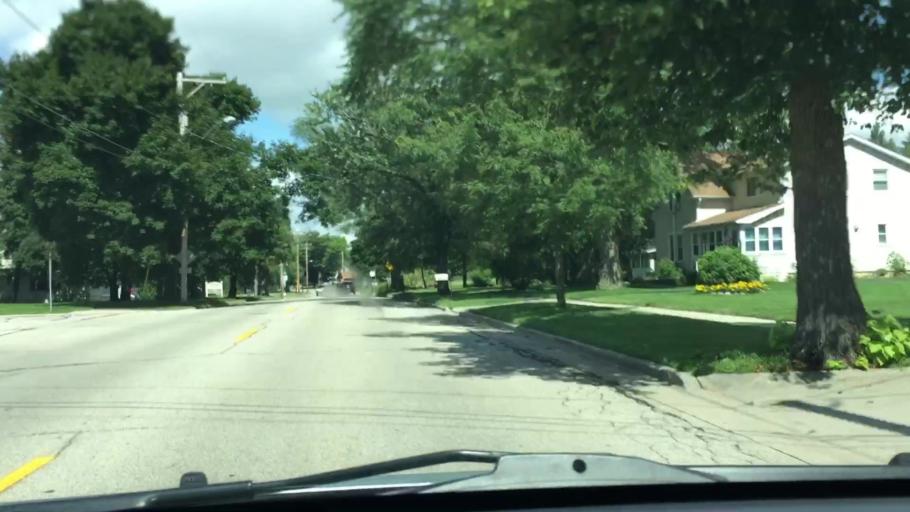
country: US
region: Wisconsin
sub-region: Waukesha County
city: Hartland
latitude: 43.1125
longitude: -88.3441
